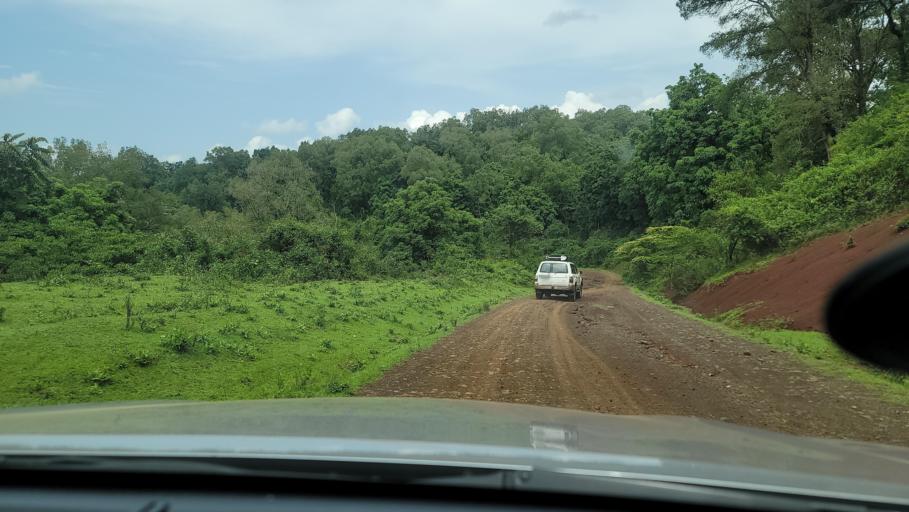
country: ET
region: Oromiya
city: Agaro
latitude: 7.7121
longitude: 36.2560
